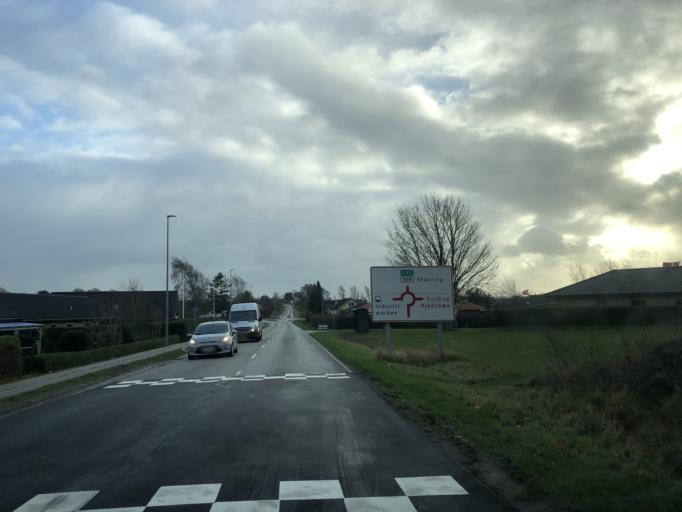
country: DK
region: North Denmark
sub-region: Rebild Kommune
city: Stovring
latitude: 56.8885
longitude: 9.7846
